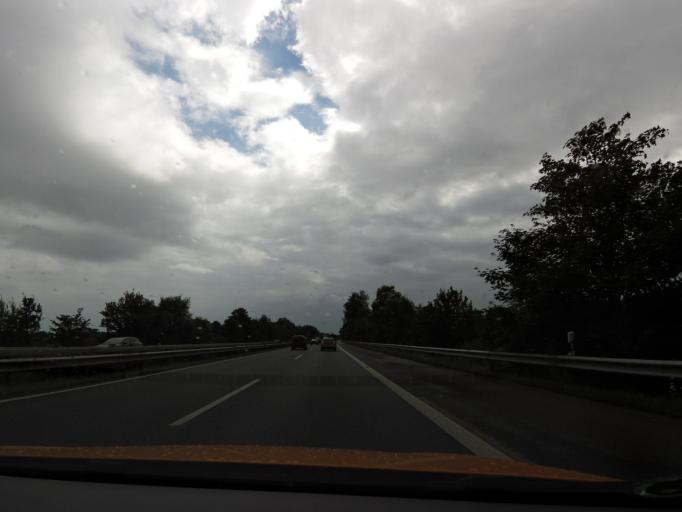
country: DE
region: Lower Saxony
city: Hatten
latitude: 53.0834
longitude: 8.3107
